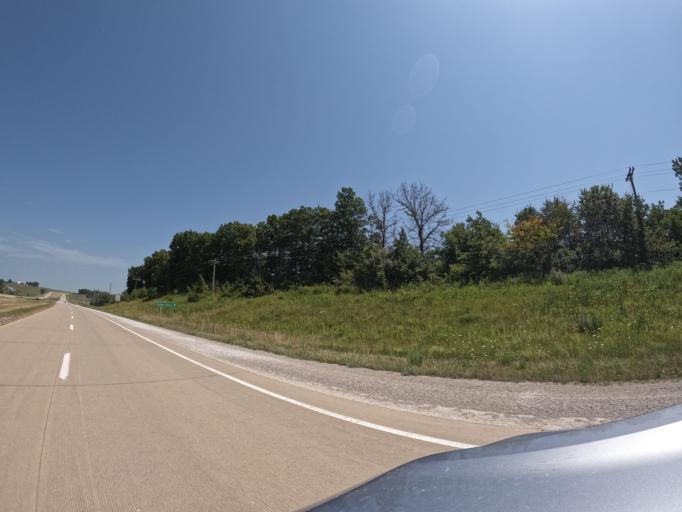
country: US
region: Iowa
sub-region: Henry County
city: Mount Pleasant
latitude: 40.9748
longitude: -91.6823
